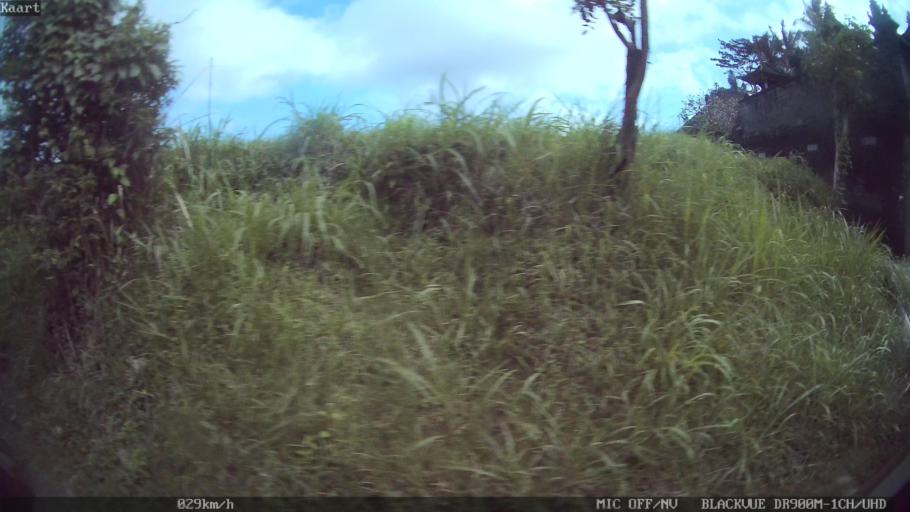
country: ID
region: Bali
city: Banjar Pesalakan
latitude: -8.4821
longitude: 115.3004
